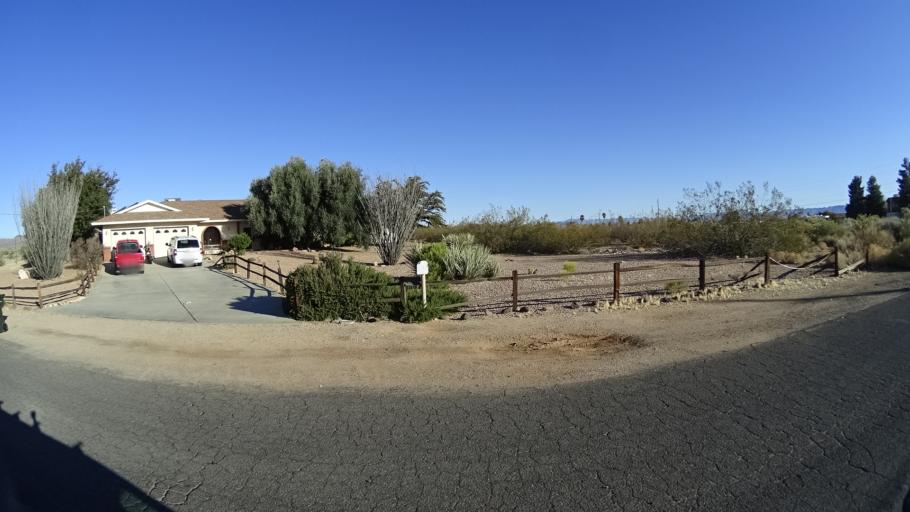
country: US
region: Arizona
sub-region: Mohave County
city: Kingman
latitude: 35.2031
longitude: -114.0007
